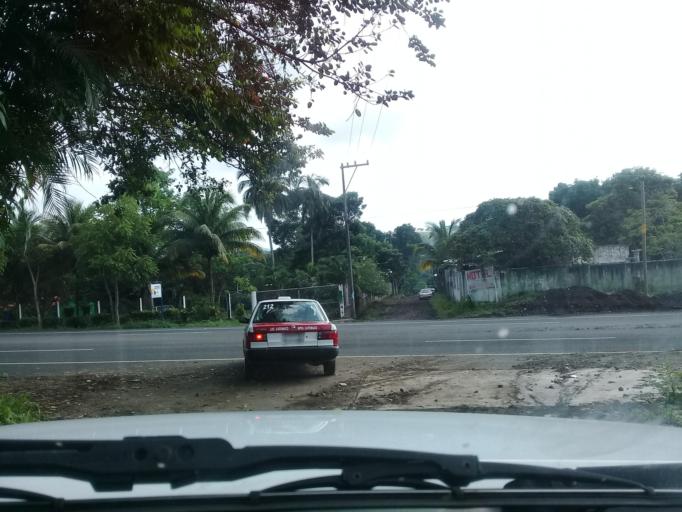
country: MX
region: Veracruz
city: Catemaco
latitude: 18.4313
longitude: -95.1300
